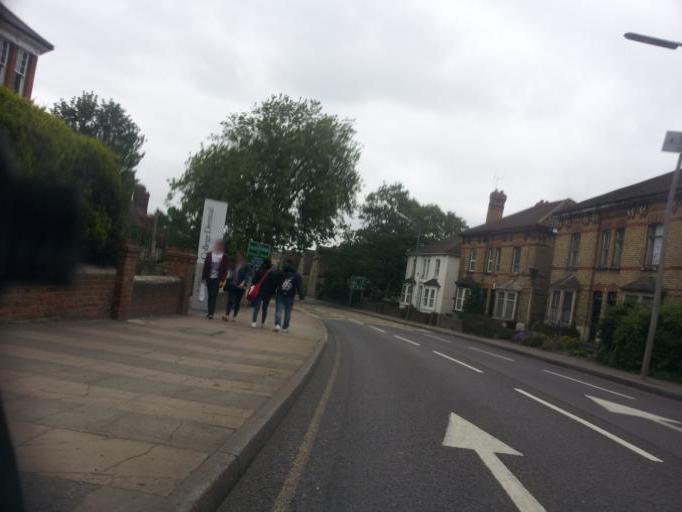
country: GB
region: England
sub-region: Kent
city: Maidstone
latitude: 51.2687
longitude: 0.5228
